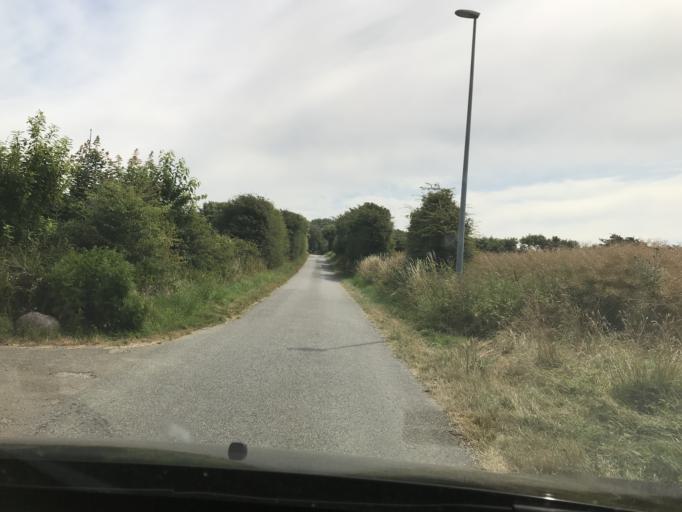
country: DK
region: South Denmark
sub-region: AEro Kommune
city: AEroskobing
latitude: 54.9174
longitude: 10.2567
